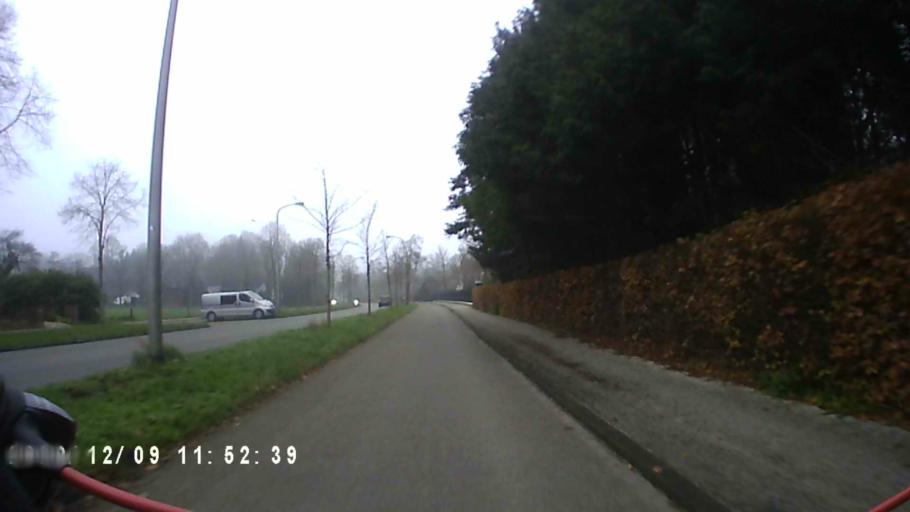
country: NL
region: Groningen
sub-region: Gemeente Haren
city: Haren
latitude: 53.1777
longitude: 6.5989
